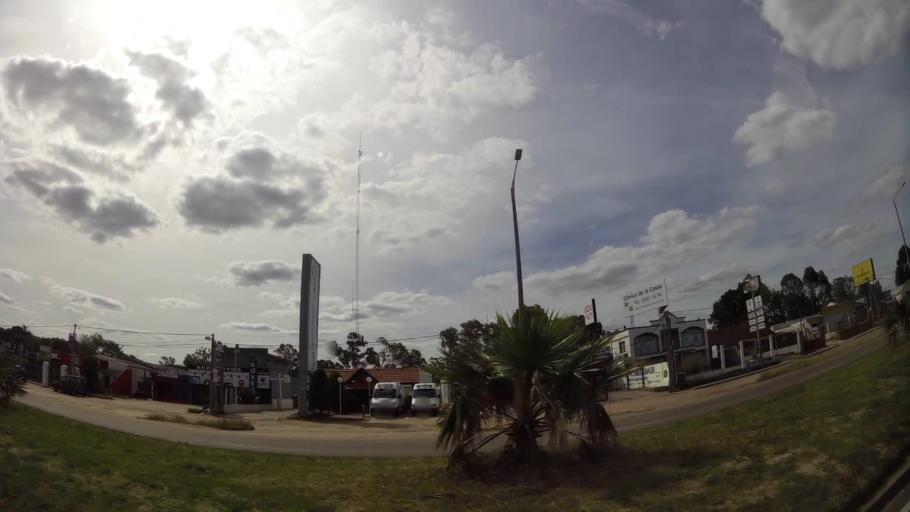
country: UY
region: Canelones
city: Barra de Carrasco
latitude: -34.8336
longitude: -55.9796
